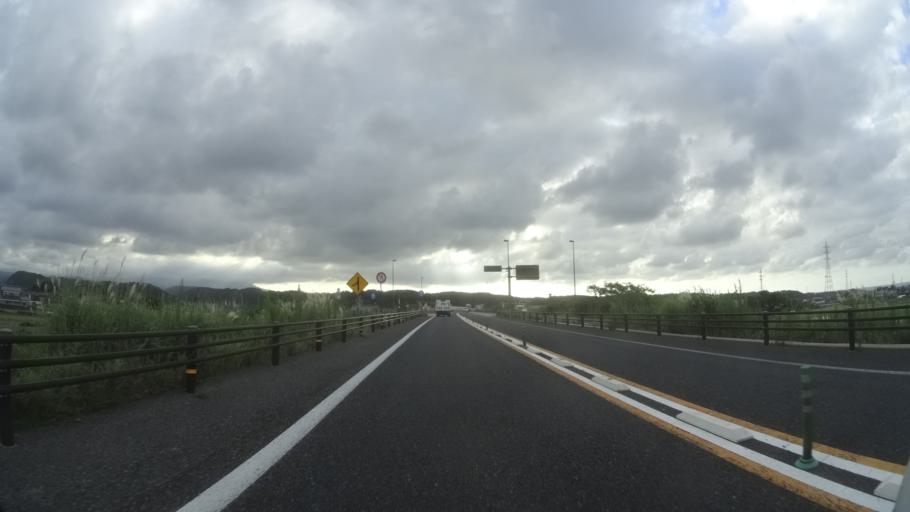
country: JP
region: Tottori
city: Kurayoshi
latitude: 35.4850
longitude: 133.6956
